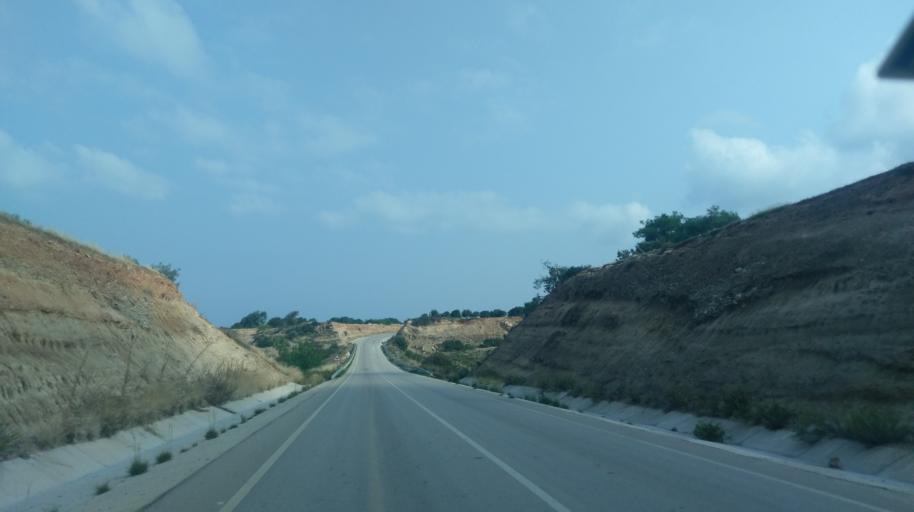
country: CY
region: Ammochostos
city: Lefkonoiko
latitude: 35.3880
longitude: 33.7290
